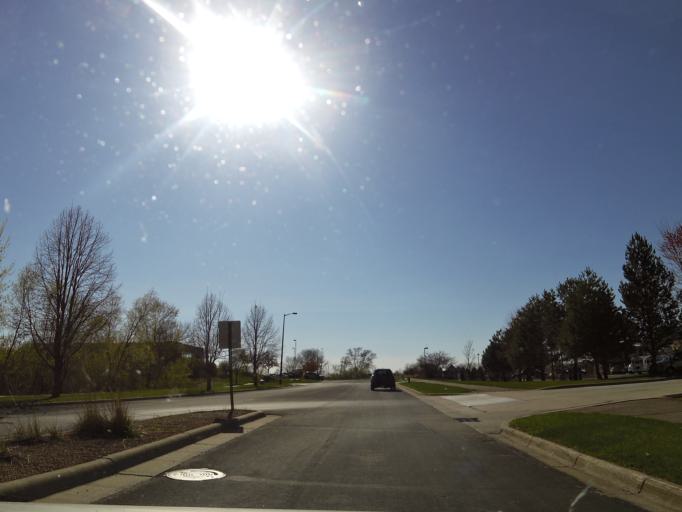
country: US
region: Minnesota
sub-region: Scott County
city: Prior Lake
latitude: 44.7456
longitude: -93.4299
